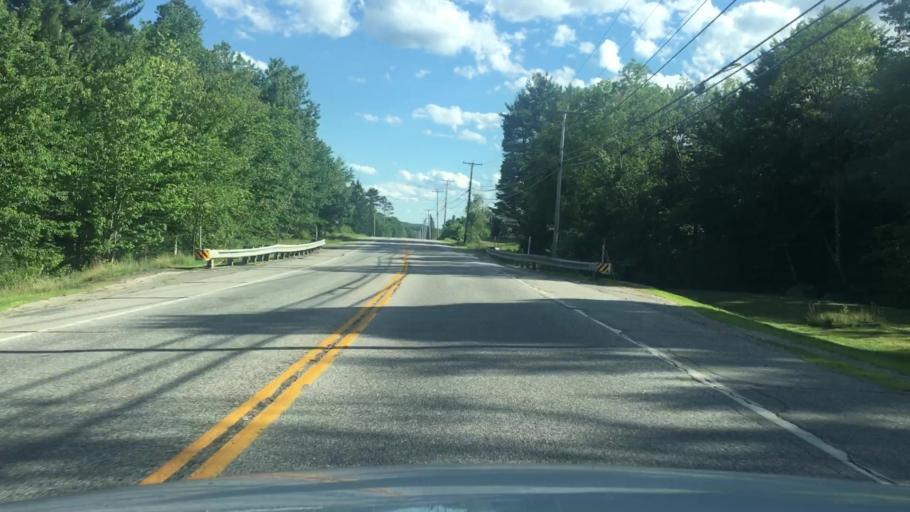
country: US
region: Maine
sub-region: Franklin County
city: Wilton
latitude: 44.5573
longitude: -70.2360
